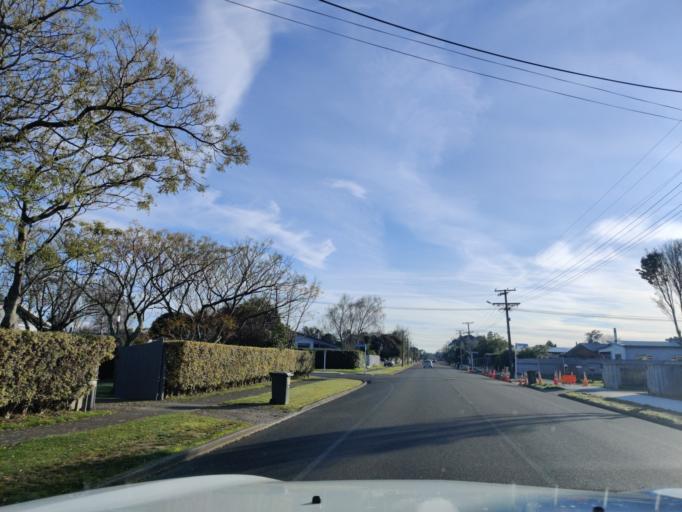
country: NZ
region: Manawatu-Wanganui
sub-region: Palmerston North City
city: Palmerston North
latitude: -40.2865
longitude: 175.7591
